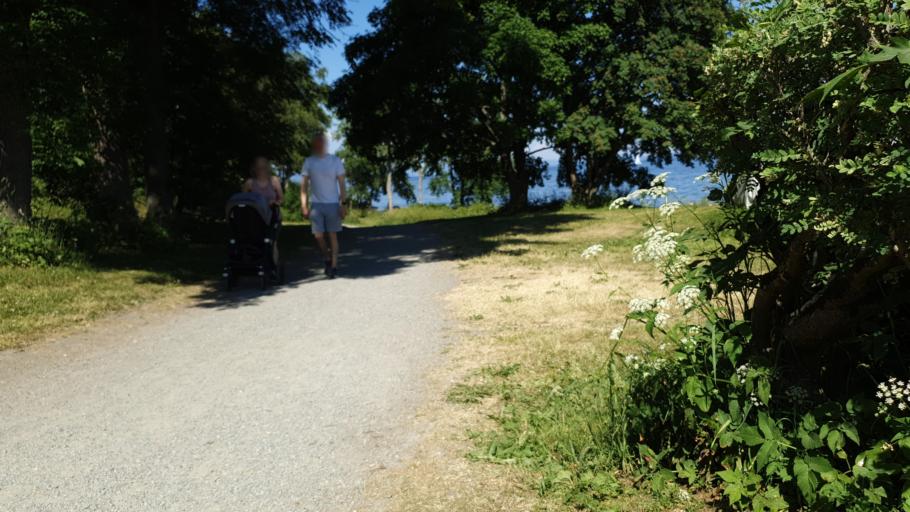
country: NO
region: Sor-Trondelag
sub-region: Trondheim
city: Trondheim
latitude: 63.4498
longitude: 10.4656
